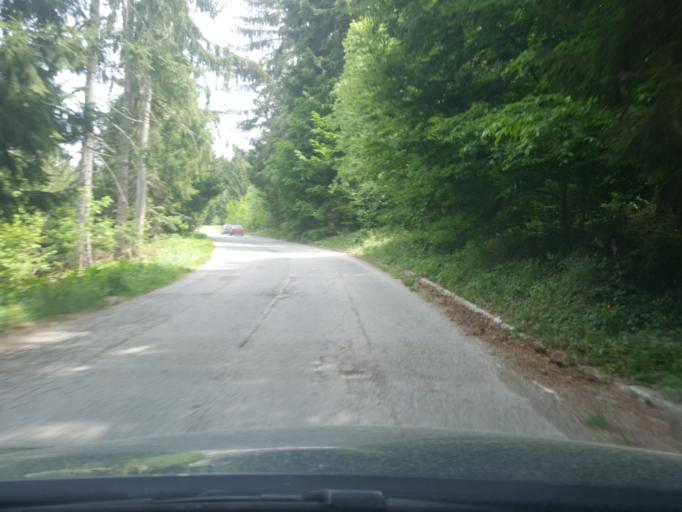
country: RS
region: Central Serbia
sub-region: Zlatiborski Okrug
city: Bajina Basta
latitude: 43.9058
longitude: 19.5064
